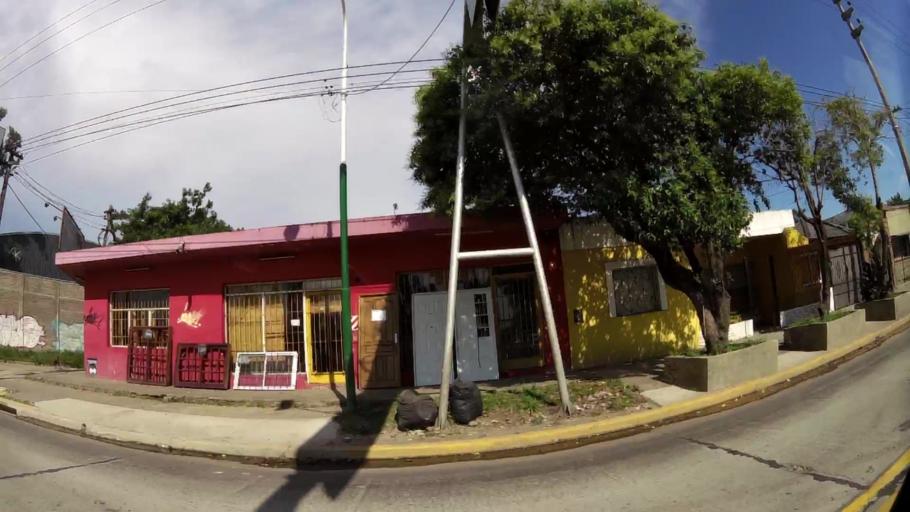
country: AR
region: Buenos Aires
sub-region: Partido de Merlo
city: Merlo
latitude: -34.6443
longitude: -58.7179
